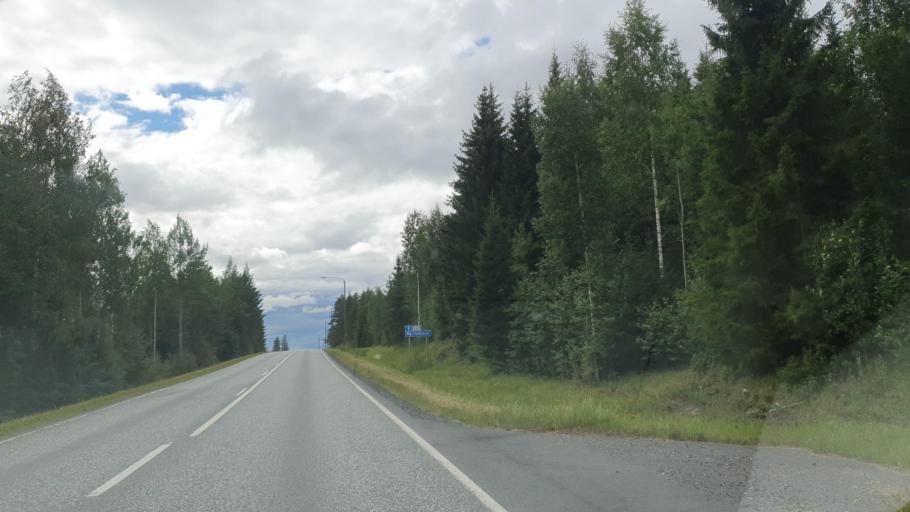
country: FI
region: Northern Savo
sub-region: Ylae-Savo
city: Iisalmi
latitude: 63.5212
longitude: 27.1772
